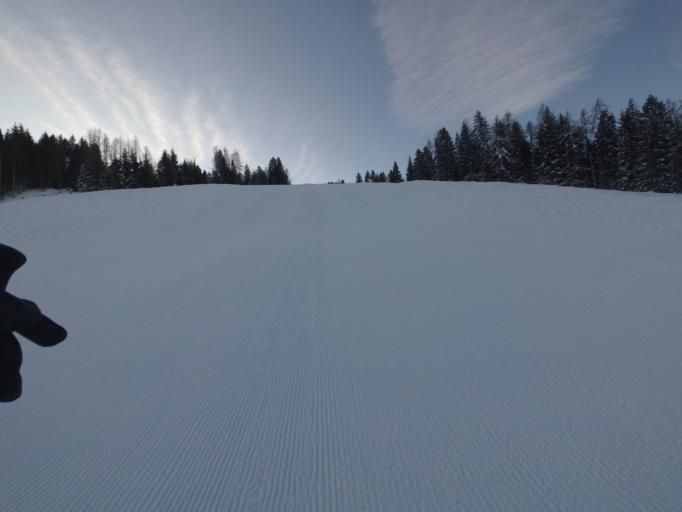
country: AT
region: Salzburg
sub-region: Politischer Bezirk Zell am See
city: Taxenbach
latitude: 47.2855
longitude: 13.0041
